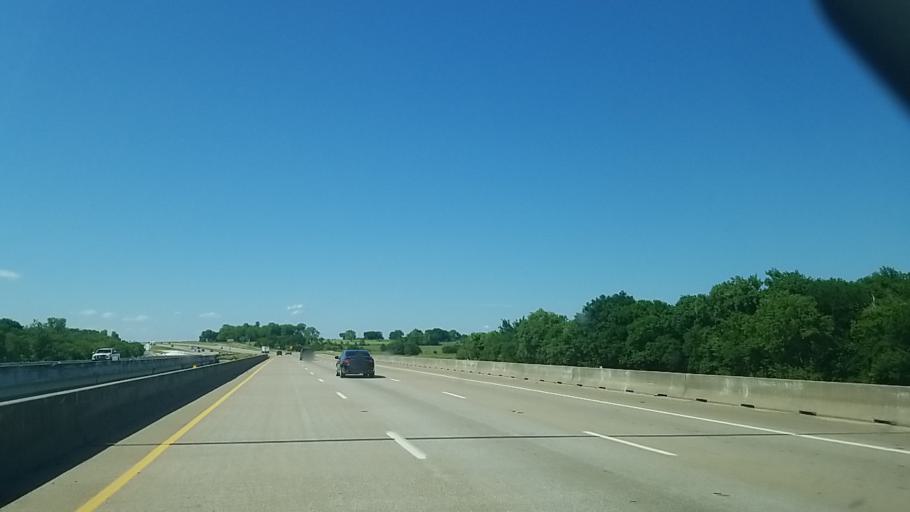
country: US
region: Texas
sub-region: Ellis County
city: Palmer
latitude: 32.4674
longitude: -96.6614
